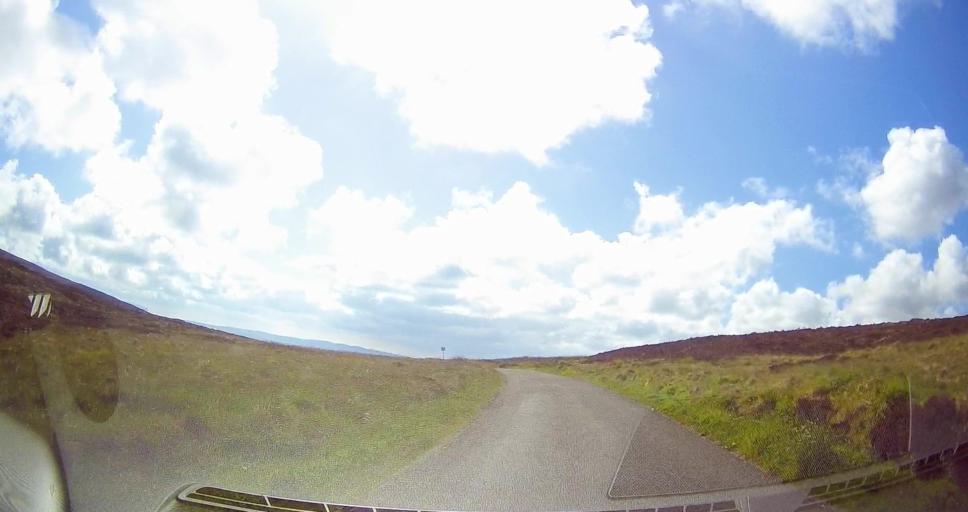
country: GB
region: Scotland
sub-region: Orkney Islands
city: Orkney
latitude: 59.0500
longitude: -3.1186
